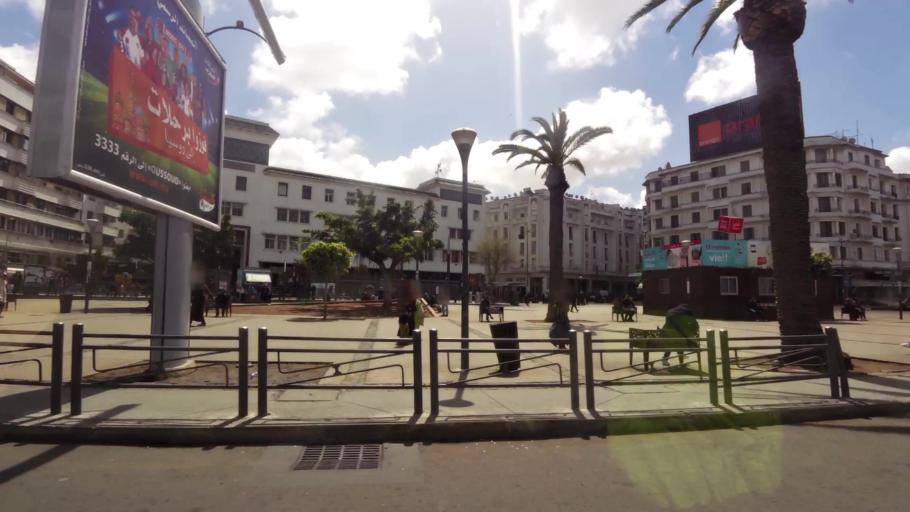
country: MA
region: Grand Casablanca
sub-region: Casablanca
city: Casablanca
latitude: 33.5953
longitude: -7.6185
